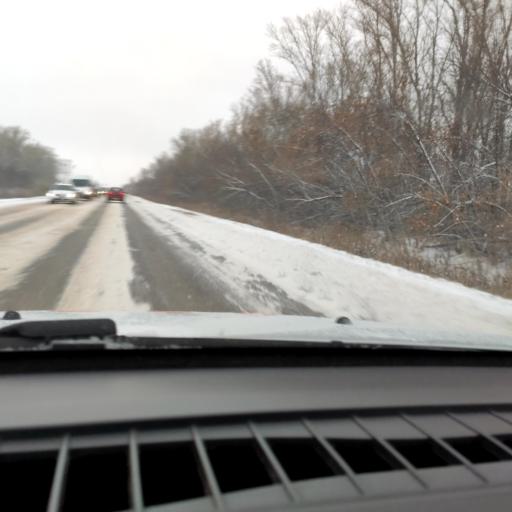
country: RU
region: Samara
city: Tol'yatti
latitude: 53.6282
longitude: 49.3047
